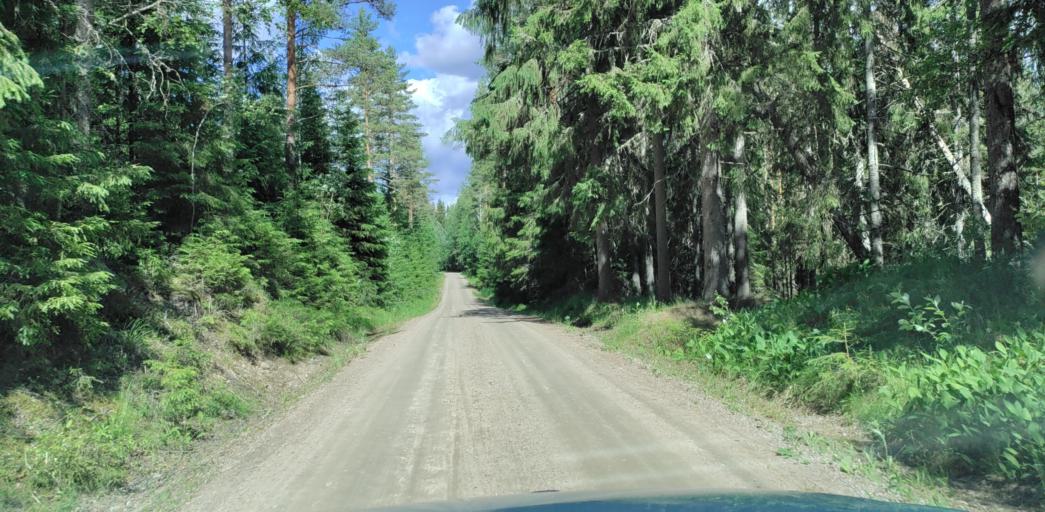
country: SE
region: Vaermland
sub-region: Sunne Kommun
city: Sunne
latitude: 60.0426
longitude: 13.2535
